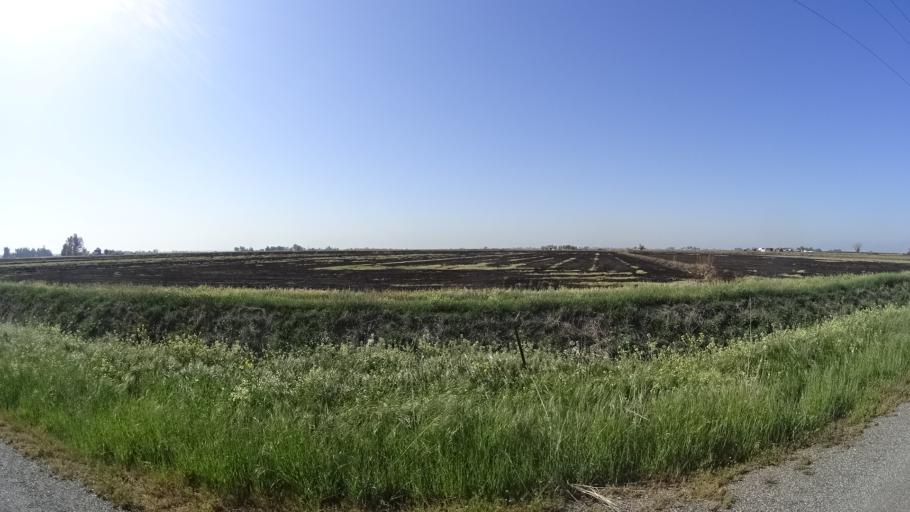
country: US
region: California
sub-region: Glenn County
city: Willows
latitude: 39.6017
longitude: -122.0727
